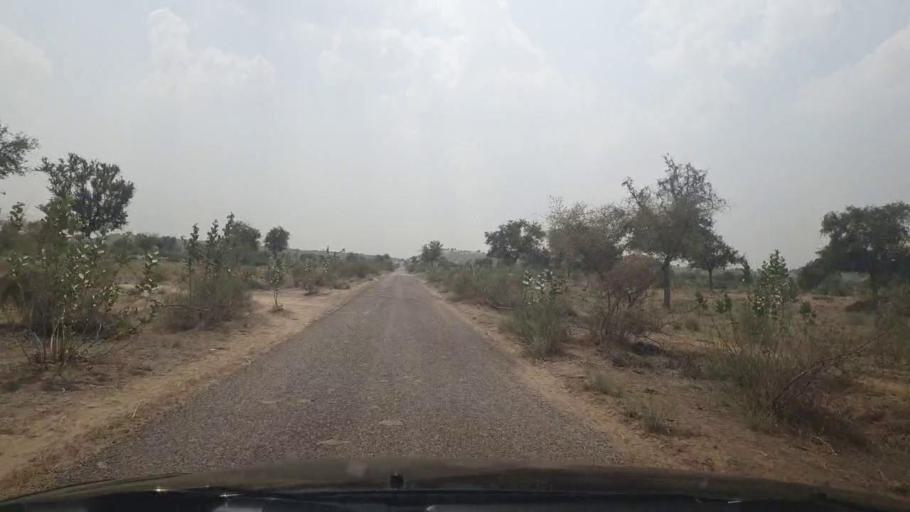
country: PK
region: Sindh
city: Islamkot
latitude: 25.0183
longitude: 70.5071
